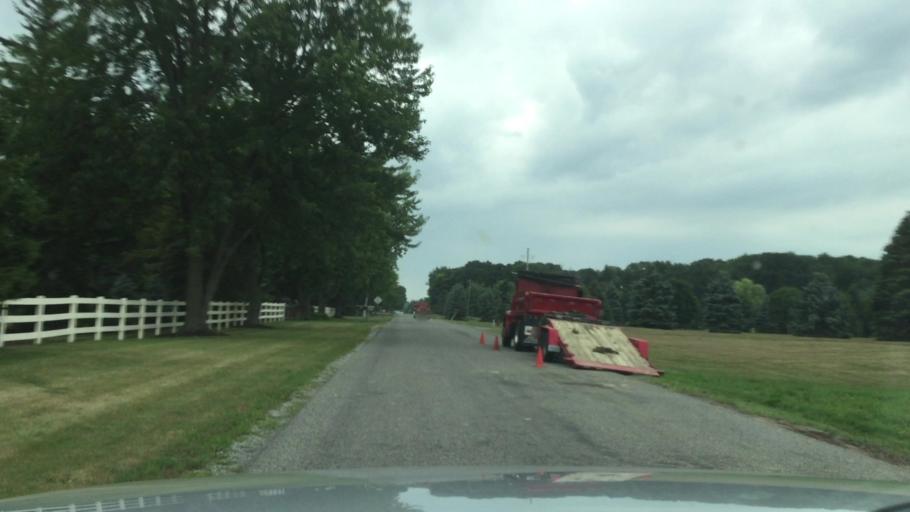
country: US
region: Michigan
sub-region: Saginaw County
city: Frankenmuth
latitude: 43.3210
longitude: -83.7958
